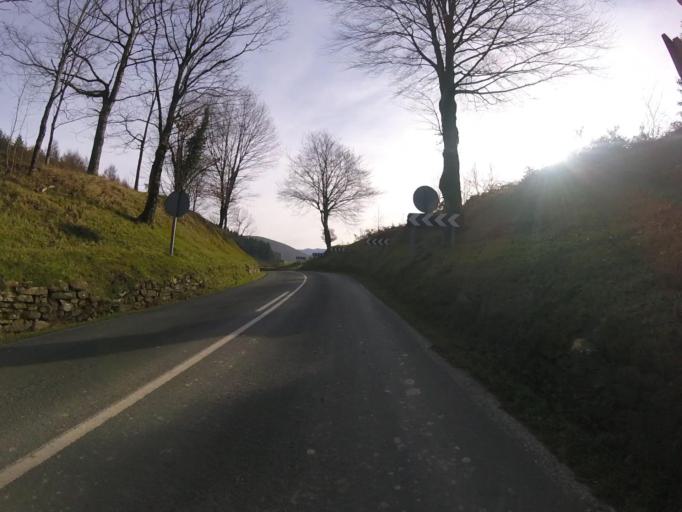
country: ES
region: Navarre
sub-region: Provincia de Navarra
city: Areso
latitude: 43.1026
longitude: -1.9556
